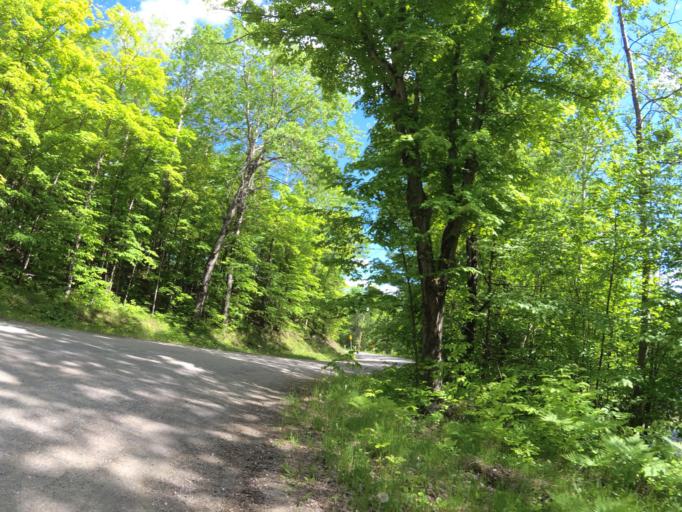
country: CA
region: Ontario
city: Renfrew
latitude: 45.0404
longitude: -76.8196
